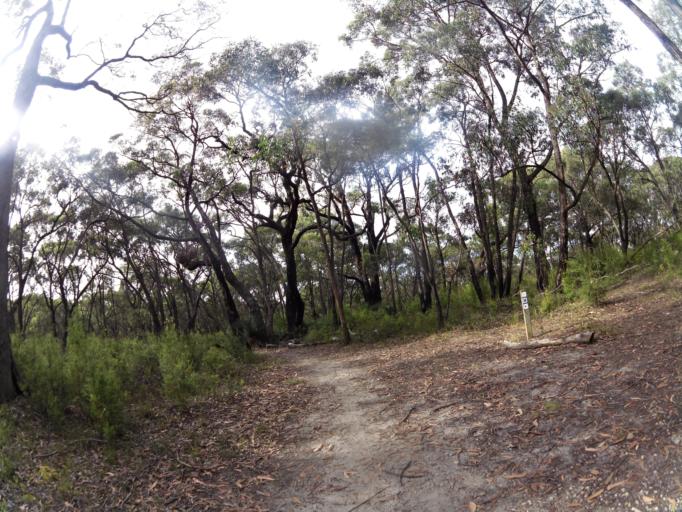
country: AU
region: Victoria
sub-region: Colac-Otway
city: Colac
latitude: -38.4973
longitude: 143.7070
